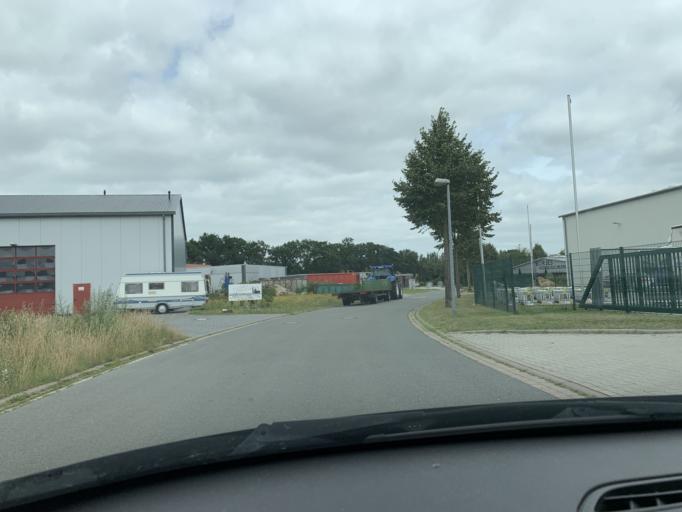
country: DE
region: Lower Saxony
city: Westerstede
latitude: 53.2674
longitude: 7.9507
